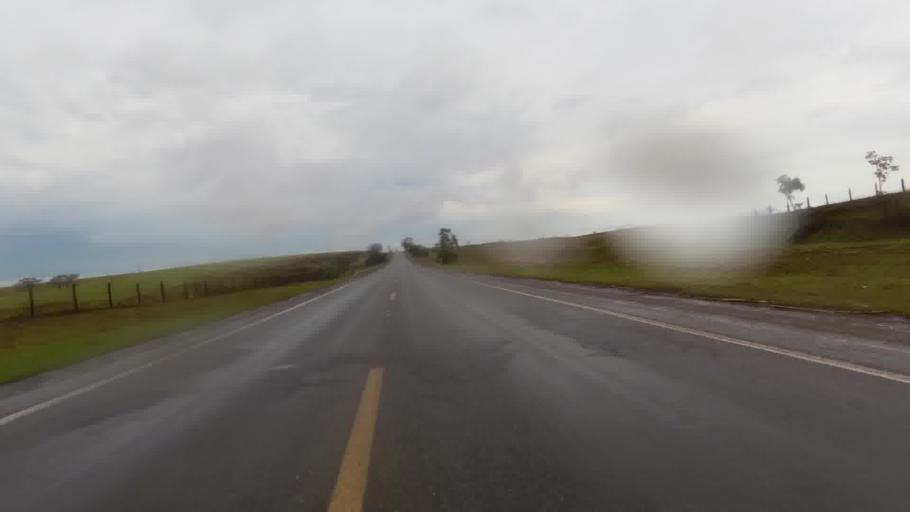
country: BR
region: Rio de Janeiro
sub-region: Campos Dos Goytacazes
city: Campos
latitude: -21.5201
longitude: -41.3344
